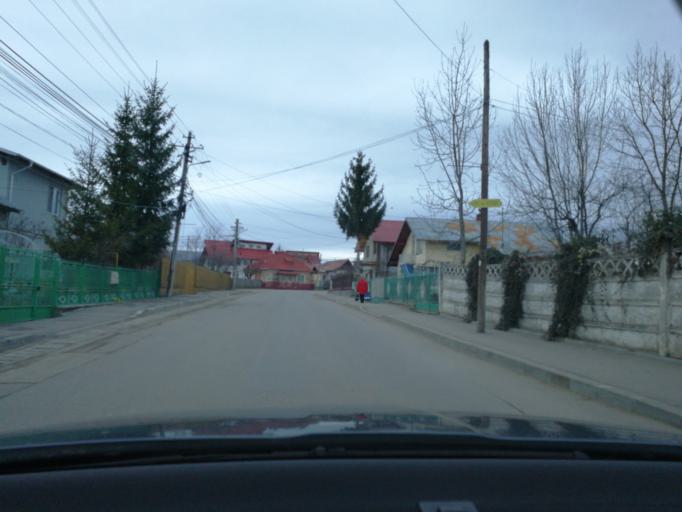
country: RO
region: Prahova
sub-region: Oras Breaza
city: Breaza
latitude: 45.1789
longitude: 25.6655
